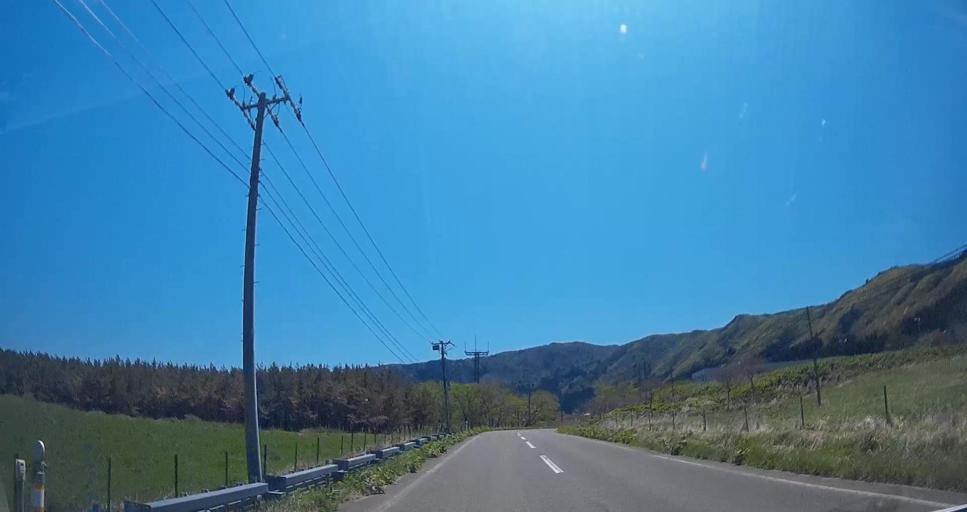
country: JP
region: Aomori
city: Mutsu
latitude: 41.4104
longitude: 141.4487
